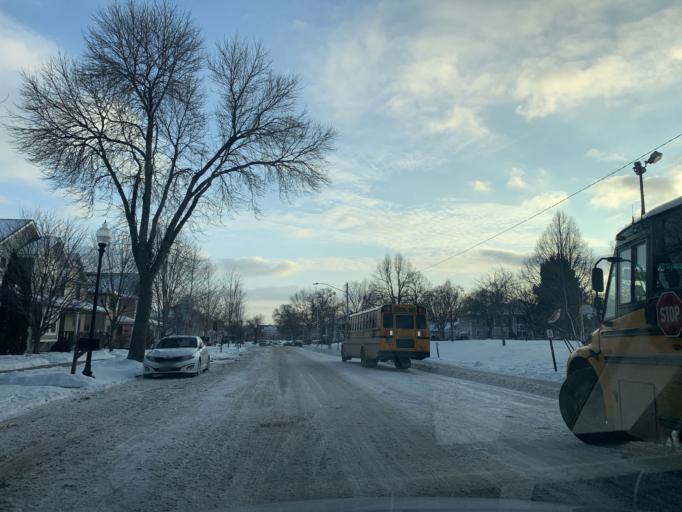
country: US
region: Minnesota
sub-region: Hennepin County
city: Minneapolis
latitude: 44.9872
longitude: -93.2941
